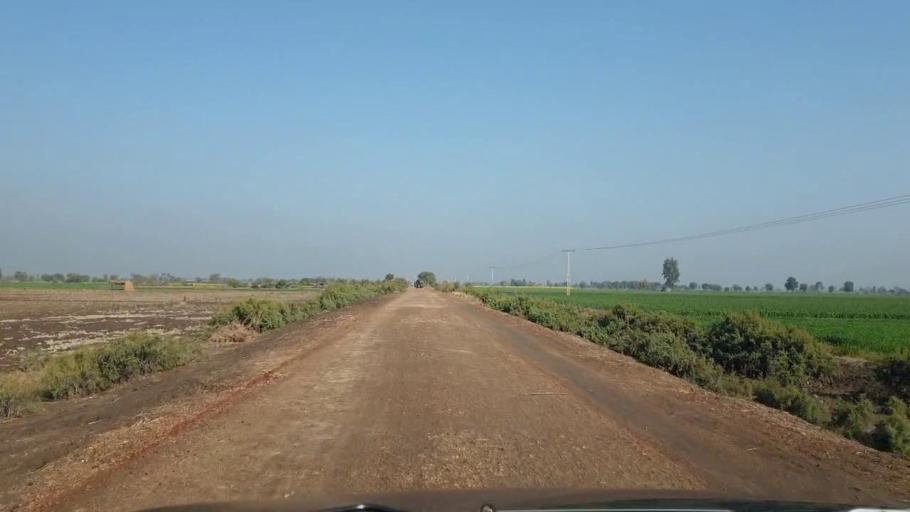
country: PK
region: Sindh
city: Sinjhoro
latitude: 26.0495
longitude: 68.7885
